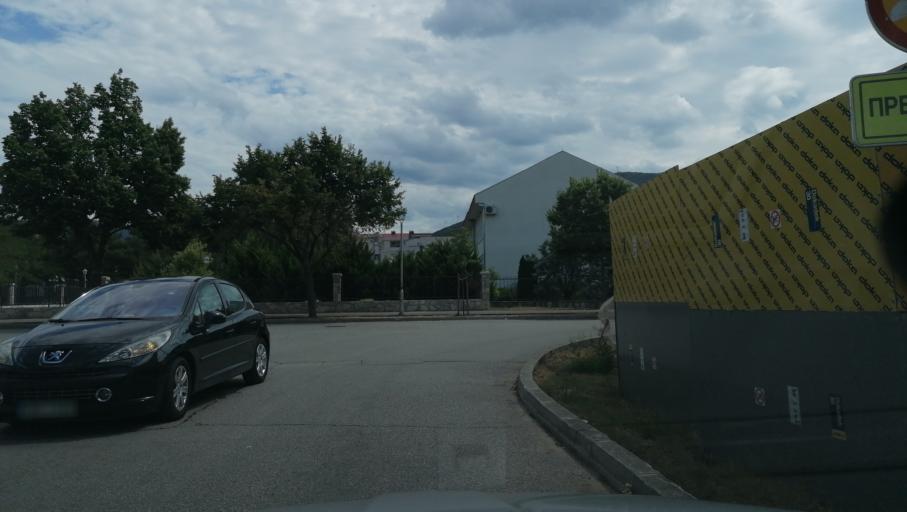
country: BA
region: Republika Srpska
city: Trebinje
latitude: 42.7079
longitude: 18.3435
